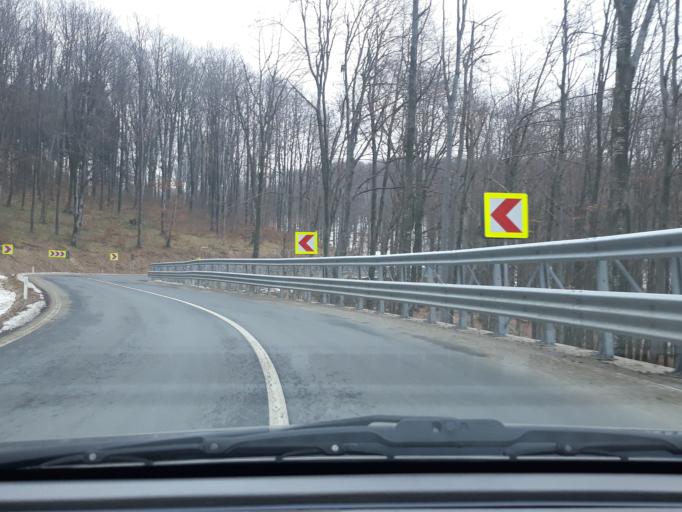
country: RO
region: Bihor
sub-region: Oras Alesd
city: Padurea Neagra
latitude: 47.1214
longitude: 22.4241
